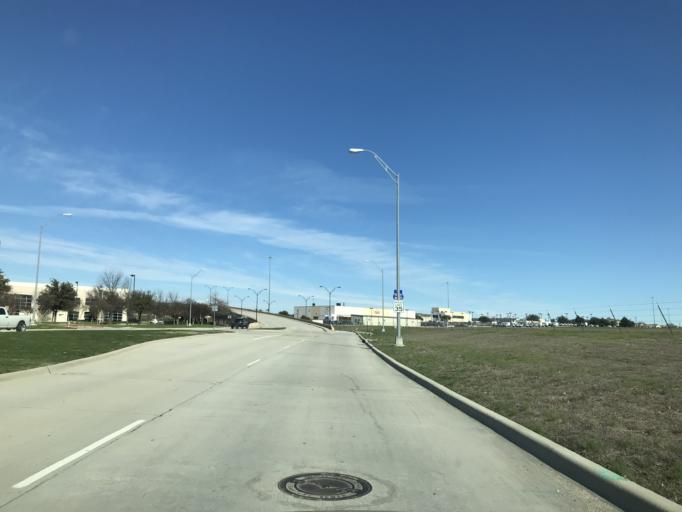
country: US
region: Texas
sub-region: Tarrant County
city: Blue Mound
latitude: 32.8359
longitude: -97.3017
